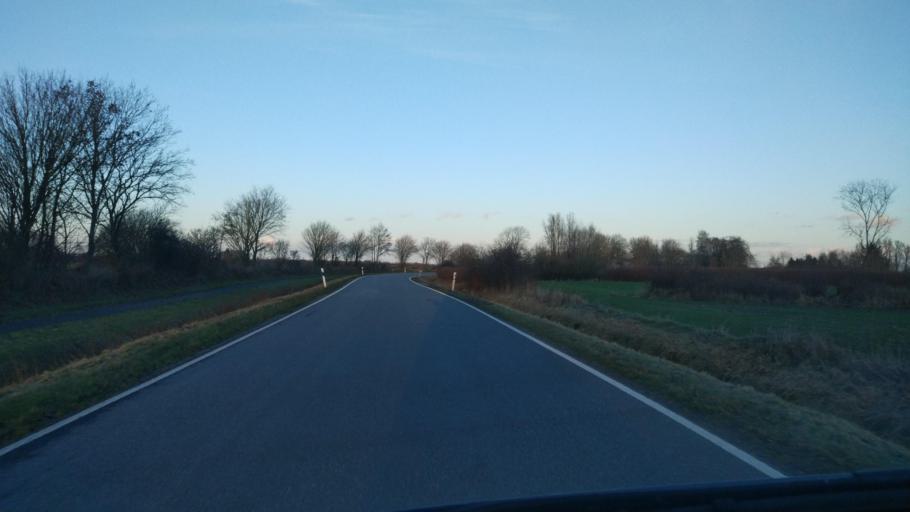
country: DE
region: Schleswig-Holstein
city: Hollingstedt
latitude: 54.4637
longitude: 9.3621
